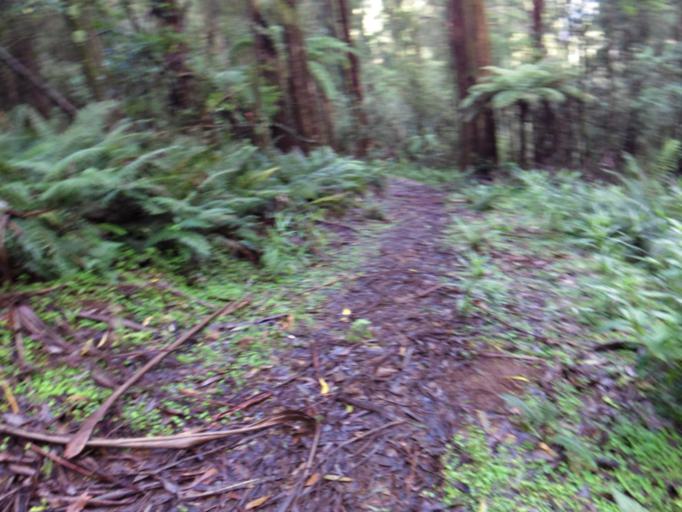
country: AU
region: Victoria
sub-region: Yarra Ranges
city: Mount Dandenong
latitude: -37.8400
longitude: 145.3498
